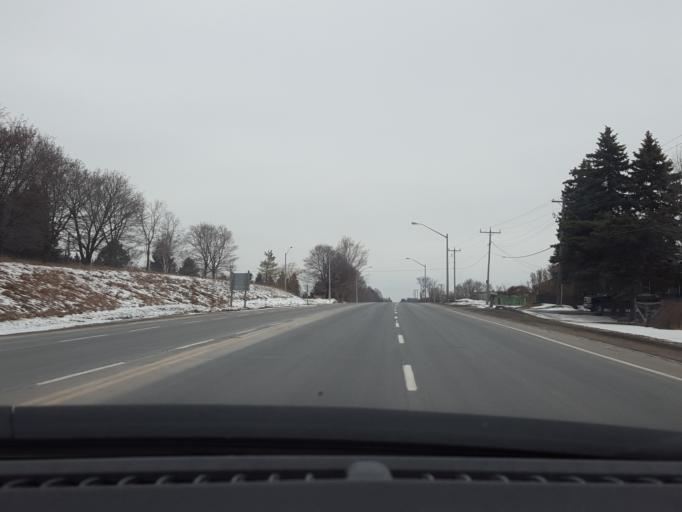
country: CA
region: Ontario
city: Newmarket
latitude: 44.1097
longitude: -79.4173
